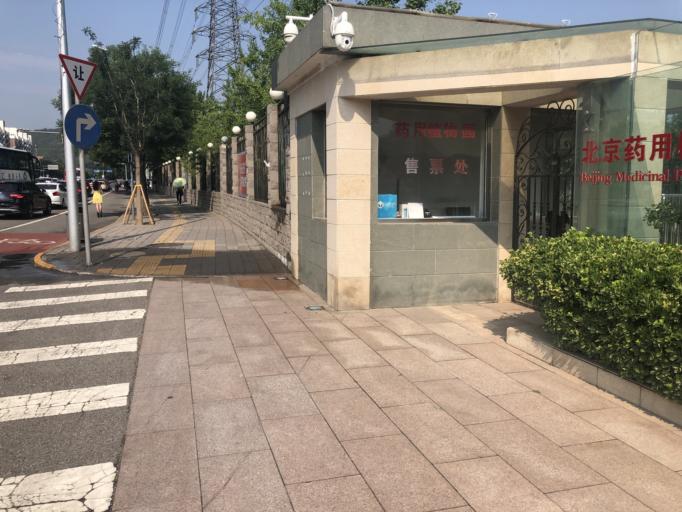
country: CN
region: Beijing
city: Xibeiwang
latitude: 40.0317
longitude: 116.2681
